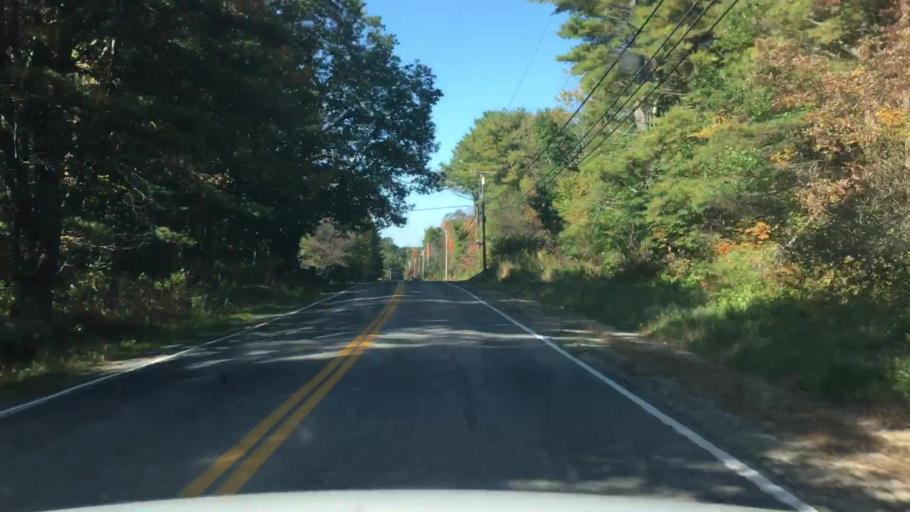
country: US
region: Maine
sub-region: Sagadahoc County
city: Topsham
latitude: 44.0338
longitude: -69.9534
